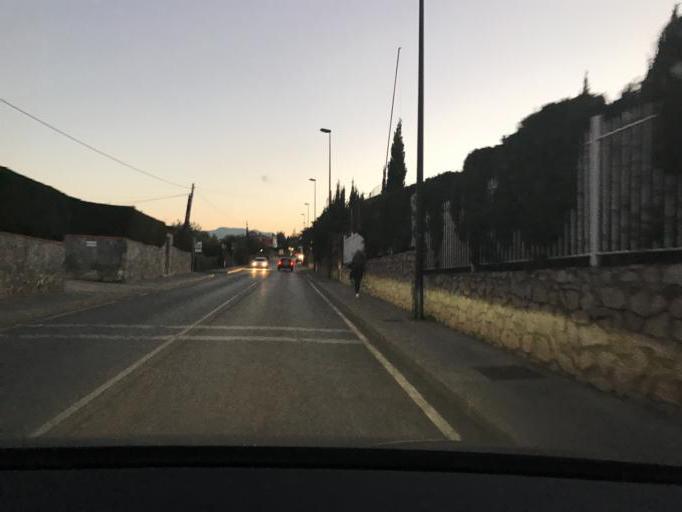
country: ES
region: Andalusia
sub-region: Provincia de Granada
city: Ogijares
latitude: 37.1140
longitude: -3.6027
